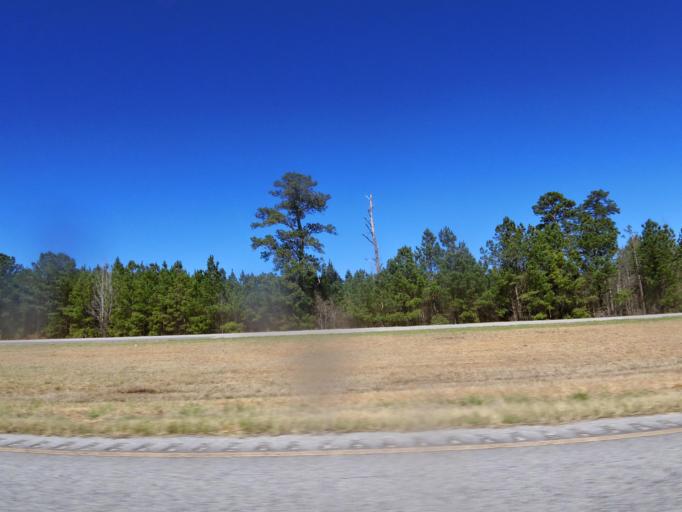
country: US
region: Alabama
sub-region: Bullock County
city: Union Springs
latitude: 32.1457
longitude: -85.6243
